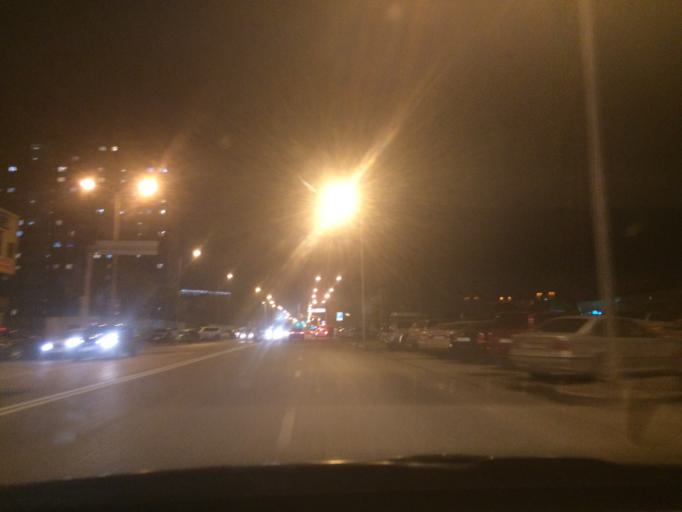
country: KZ
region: Astana Qalasy
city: Astana
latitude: 51.1619
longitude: 71.4558
